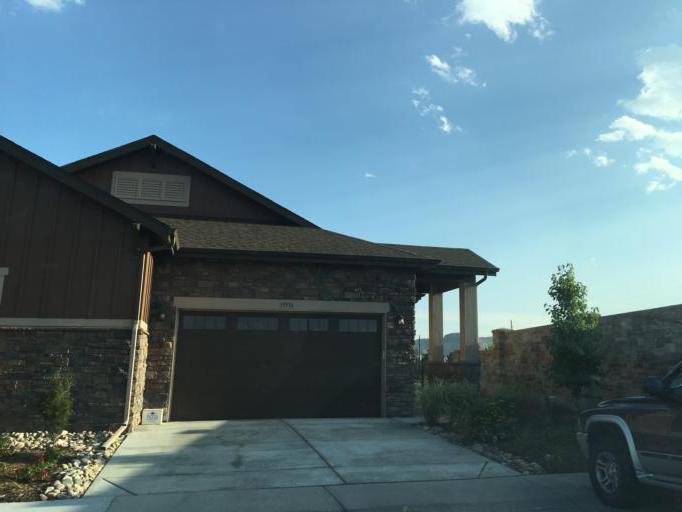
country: US
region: Colorado
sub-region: Jefferson County
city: Applewood
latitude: 39.7861
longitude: -105.1742
